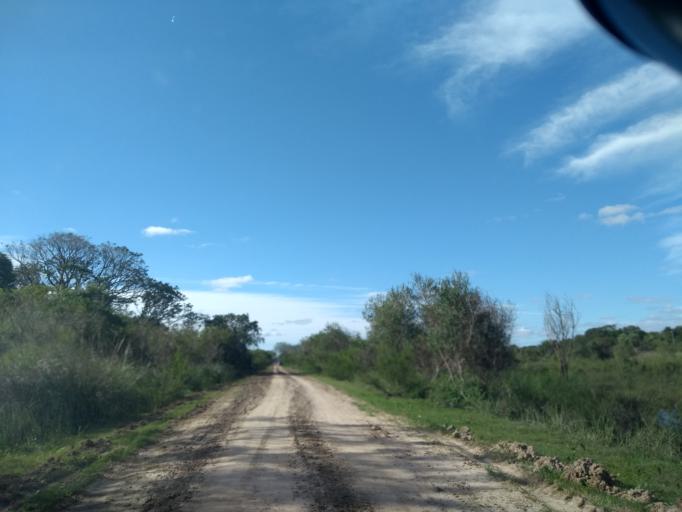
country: AR
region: Chaco
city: Margarita Belen
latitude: -27.2810
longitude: -58.9245
